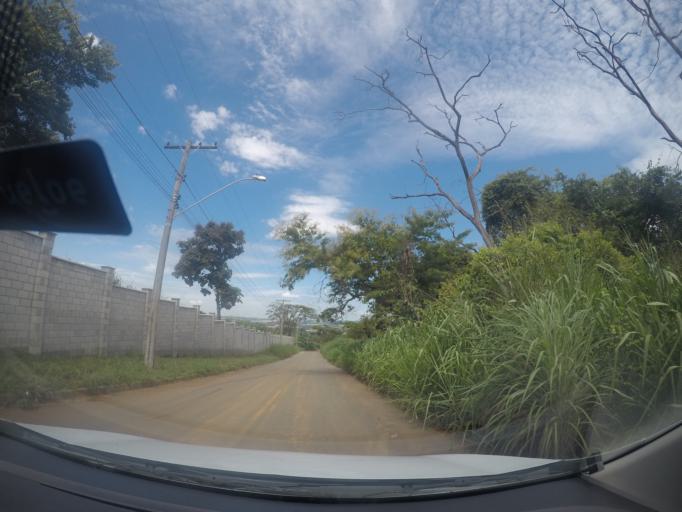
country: BR
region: Goias
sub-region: Goiania
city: Goiania
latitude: -16.6651
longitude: -49.3464
